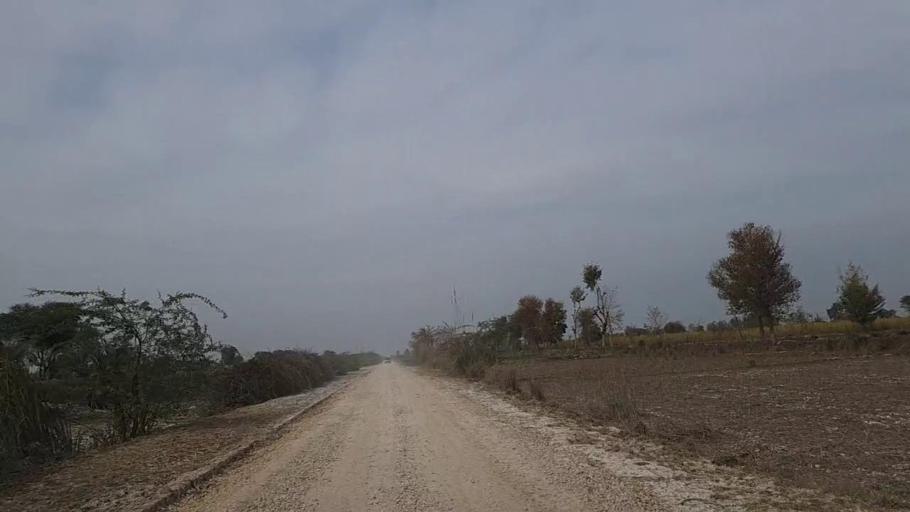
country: PK
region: Sindh
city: Daur
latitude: 26.4096
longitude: 68.4327
